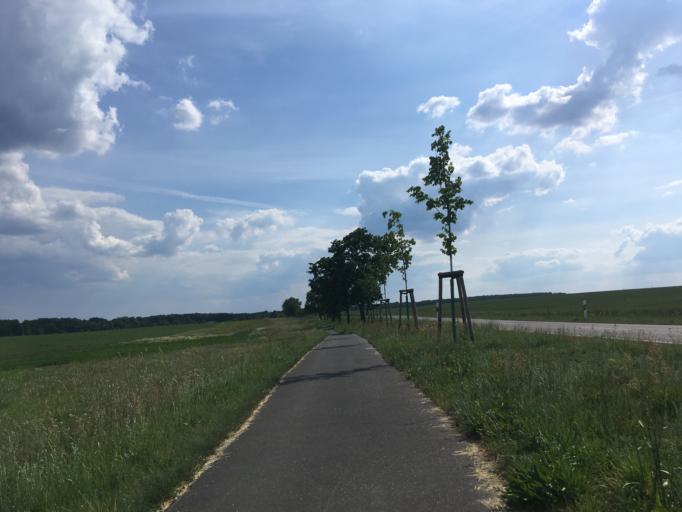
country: DE
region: Brandenburg
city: Steinhofel
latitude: 52.4107
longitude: 14.1030
